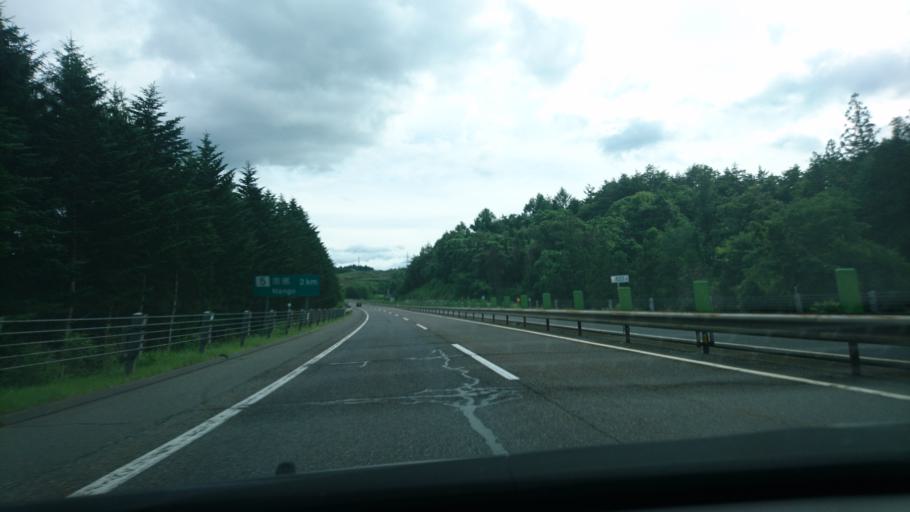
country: JP
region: Aomori
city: Hachinohe
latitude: 40.4267
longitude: 141.4399
